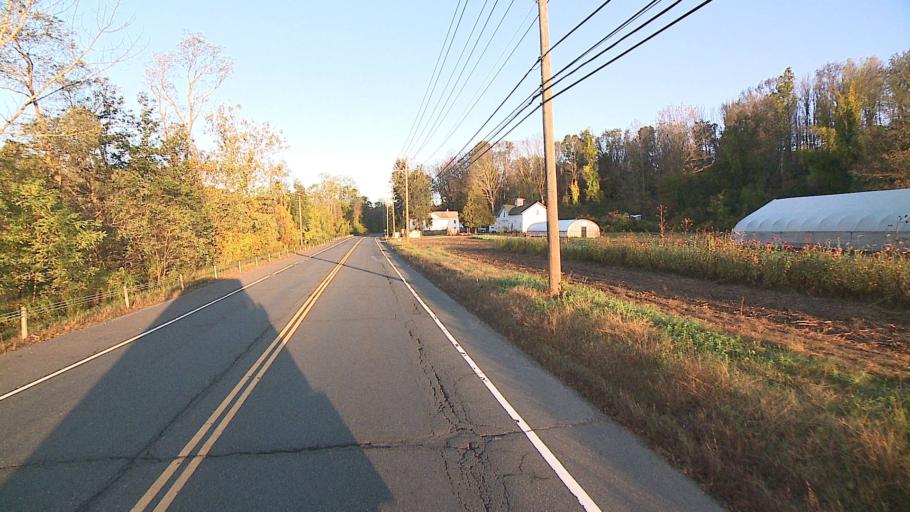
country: US
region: Connecticut
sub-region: Hartford County
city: Collinsville
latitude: 41.8402
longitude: -72.9349
